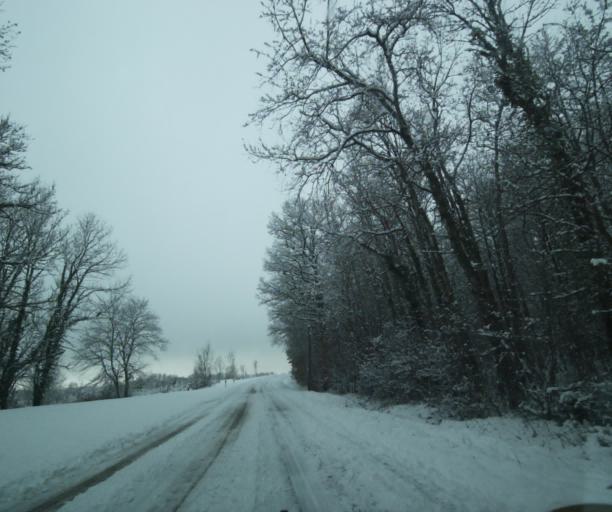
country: FR
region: Champagne-Ardenne
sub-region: Departement de la Haute-Marne
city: Montier-en-Der
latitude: 48.5432
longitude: 4.8023
